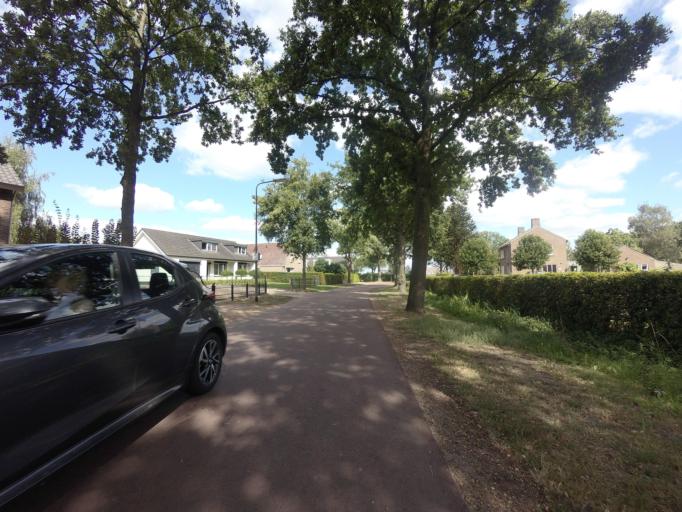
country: NL
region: North Brabant
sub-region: Gemeente Oss
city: Berghem
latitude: 51.7779
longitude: 5.5952
